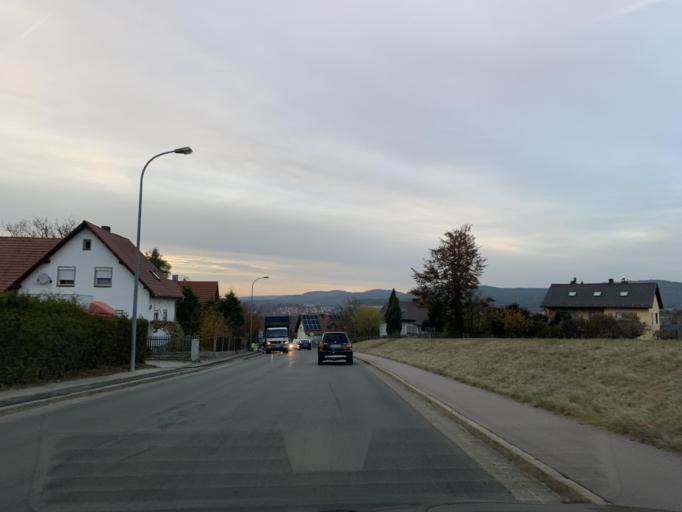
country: DE
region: Bavaria
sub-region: Upper Palatinate
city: Neunburg vorm Wald
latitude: 49.3418
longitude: 12.3924
